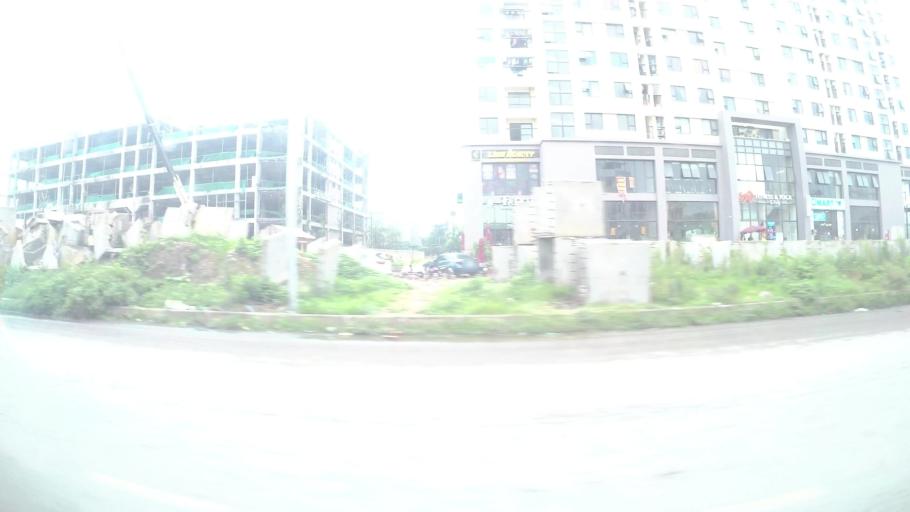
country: VN
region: Ha Noi
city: Van Dien
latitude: 20.9676
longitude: 105.8679
